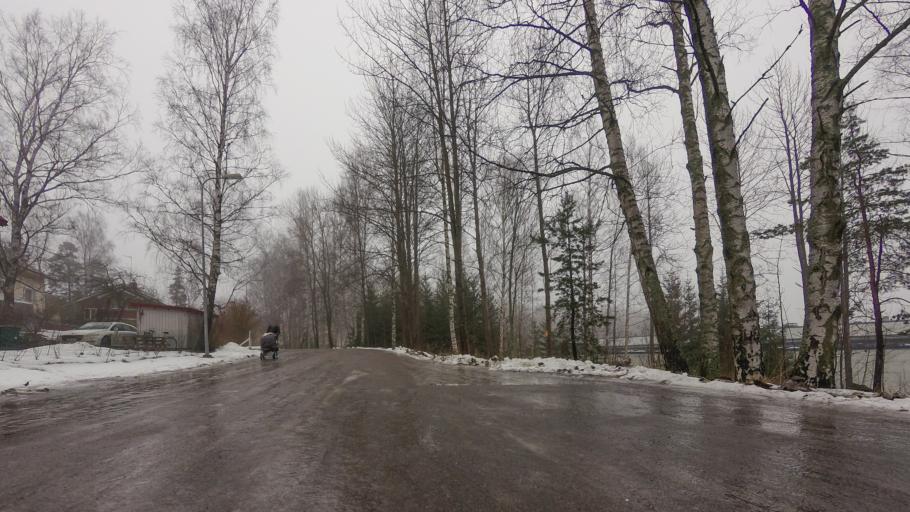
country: FI
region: Uusimaa
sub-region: Helsinki
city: Vantaa
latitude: 60.2128
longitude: 25.0467
